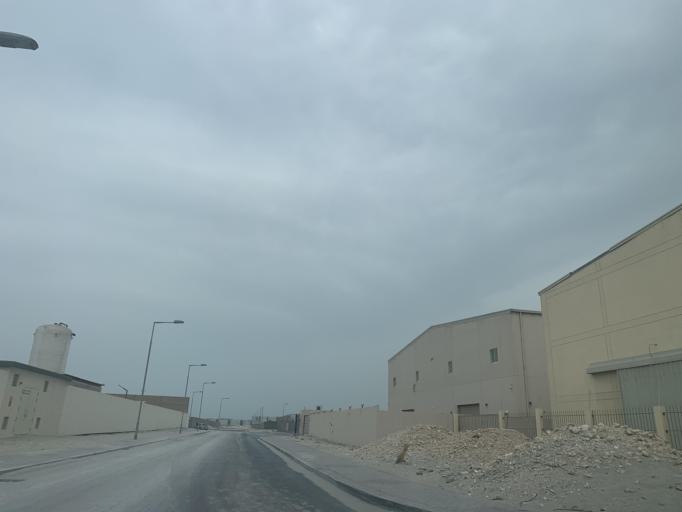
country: BH
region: Muharraq
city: Al Hadd
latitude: 26.2148
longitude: 50.6805
